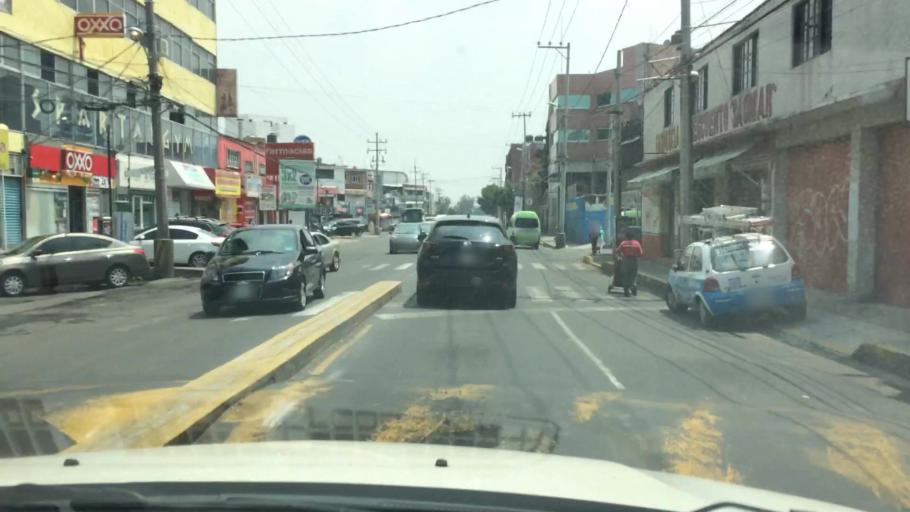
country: MX
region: Mexico City
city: Tlalpan
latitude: 19.3059
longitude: -99.1615
